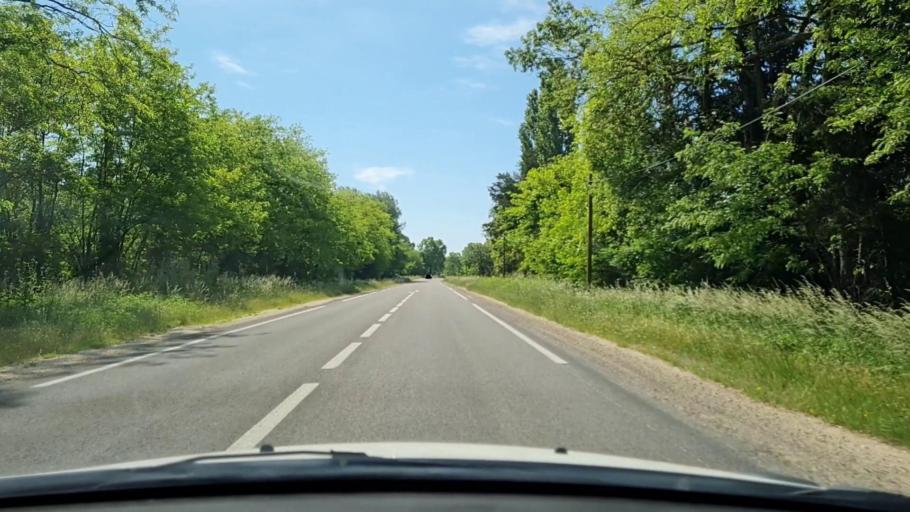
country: FR
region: Languedoc-Roussillon
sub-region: Departement du Gard
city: Saint-Genies-de-Malgoires
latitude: 43.9554
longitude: 4.2435
